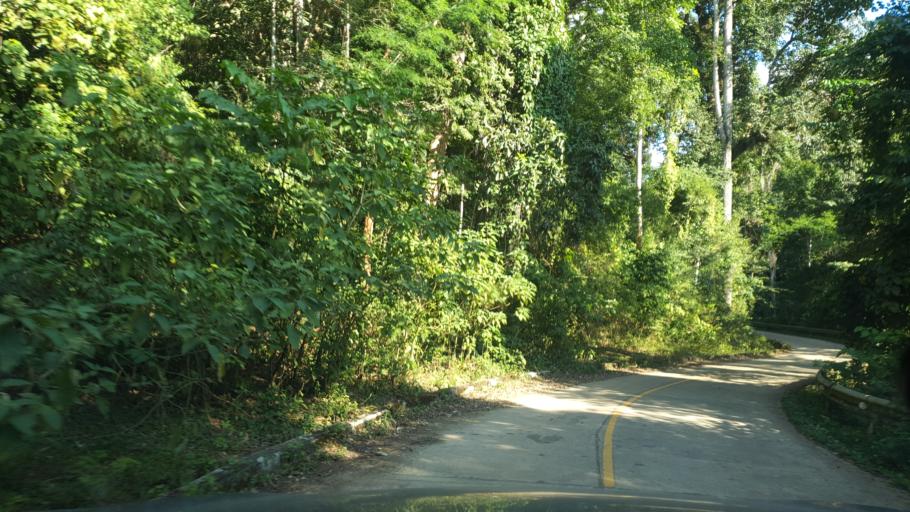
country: TH
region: Chiang Mai
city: Wiang Haeng
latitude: 19.3795
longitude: 98.7449
